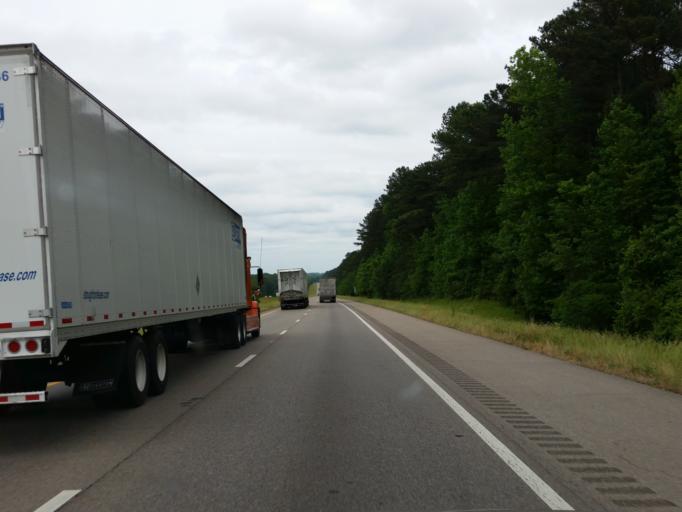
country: US
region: Mississippi
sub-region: Lauderdale County
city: Marion
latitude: 32.4057
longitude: -88.5467
